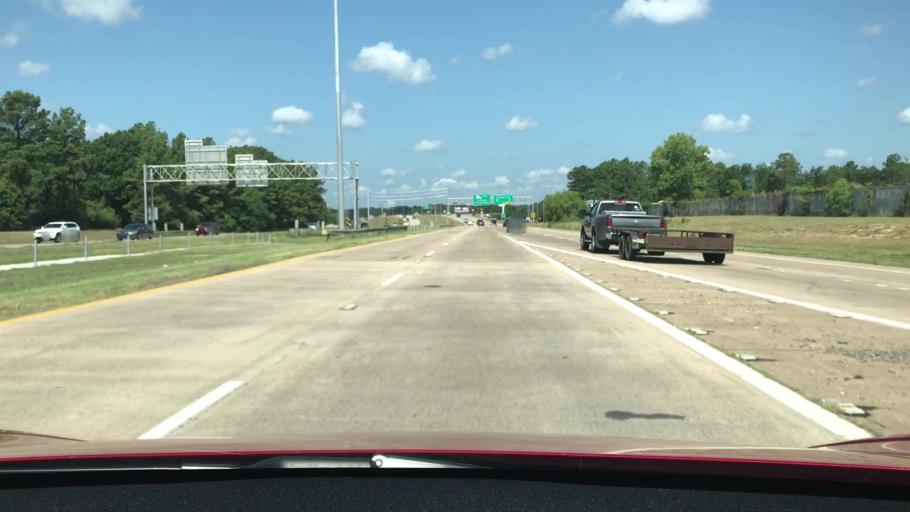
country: US
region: Louisiana
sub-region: Bossier Parish
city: Bossier City
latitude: 32.4201
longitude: -93.7557
